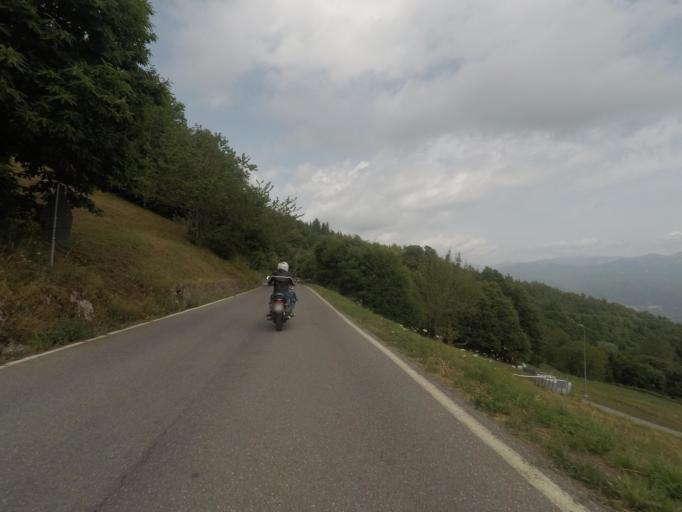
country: IT
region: Tuscany
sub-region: Provincia di Lucca
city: Careggine
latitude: 44.1073
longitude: 10.3618
